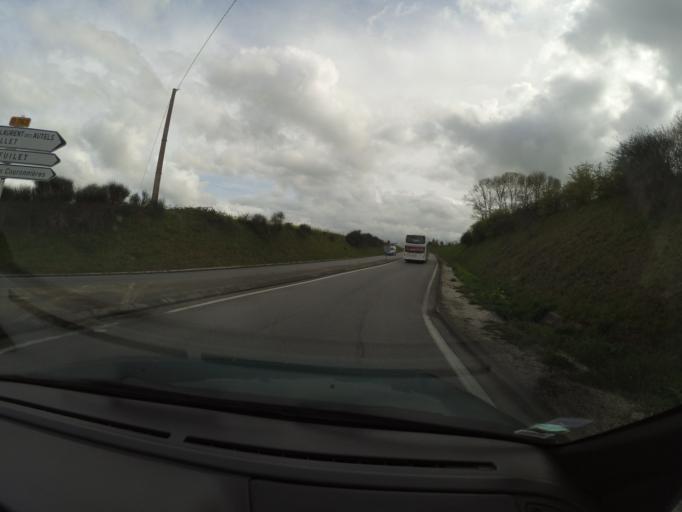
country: FR
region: Pays de la Loire
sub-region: Departement de Maine-et-Loire
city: Lire
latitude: 47.3301
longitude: -1.1677
